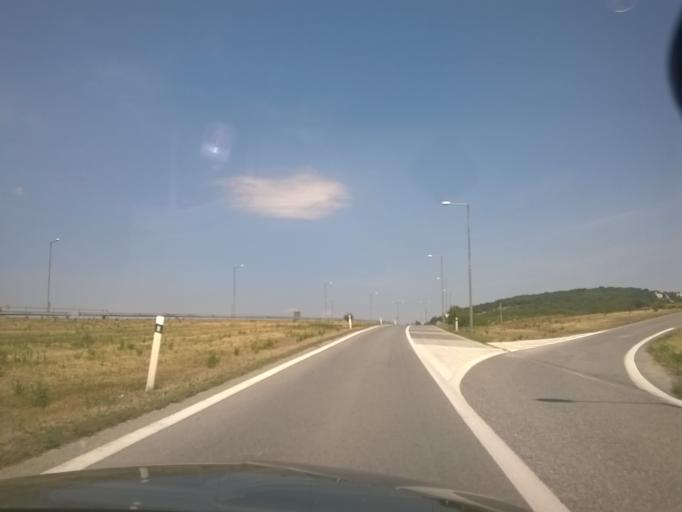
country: SK
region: Nitriansky
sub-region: Okres Nitra
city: Nitra
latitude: 48.3292
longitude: 18.0812
